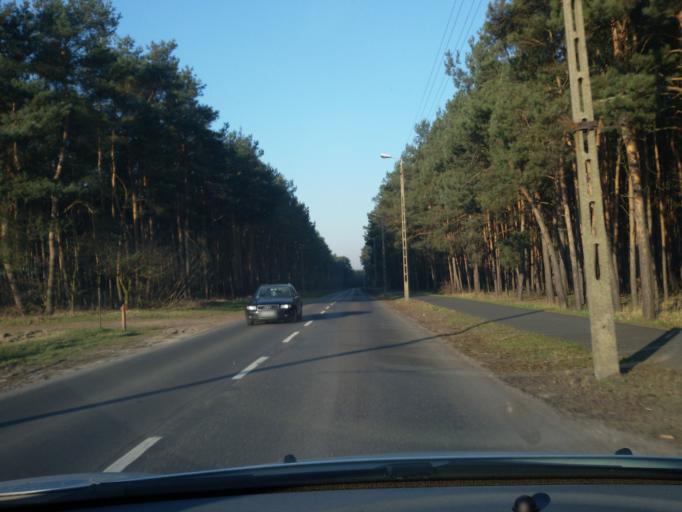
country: PL
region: Greater Poland Voivodeship
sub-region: Leszno
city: Leszno
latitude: 51.8328
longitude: 16.5647
